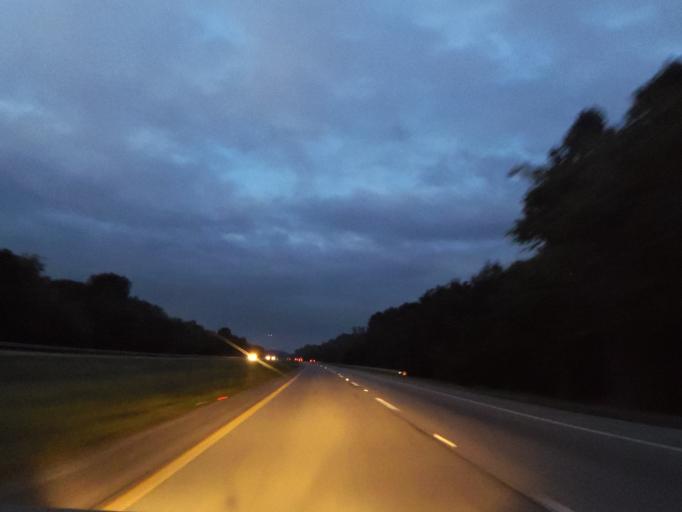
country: US
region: Alabama
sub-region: Jackson County
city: Scottsboro
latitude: 34.6174
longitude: -86.2128
